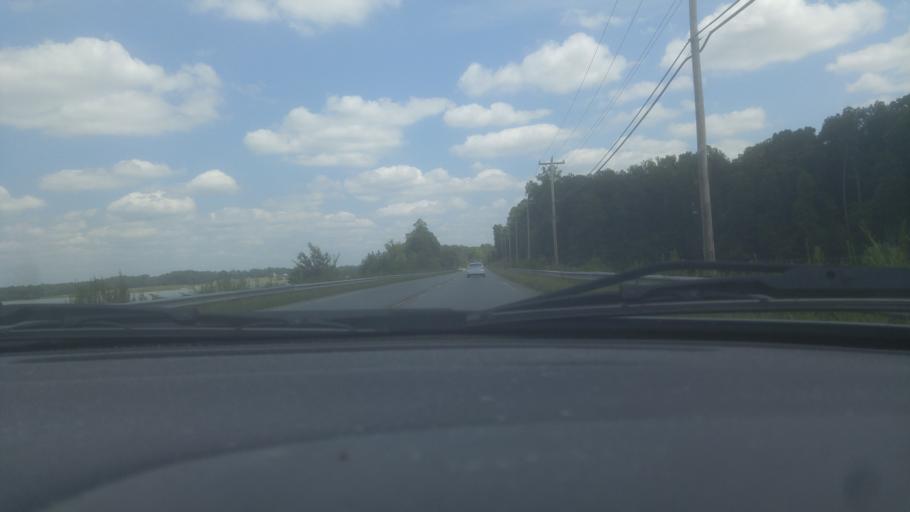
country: US
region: North Carolina
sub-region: Rowan County
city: Enochville
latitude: 35.4382
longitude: -80.7128
